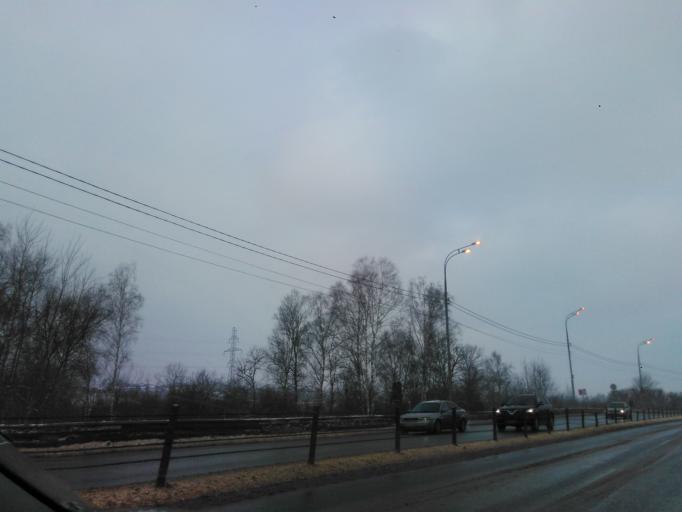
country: RU
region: Moskovskaya
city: Dedenevo
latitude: 56.2686
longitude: 37.5022
